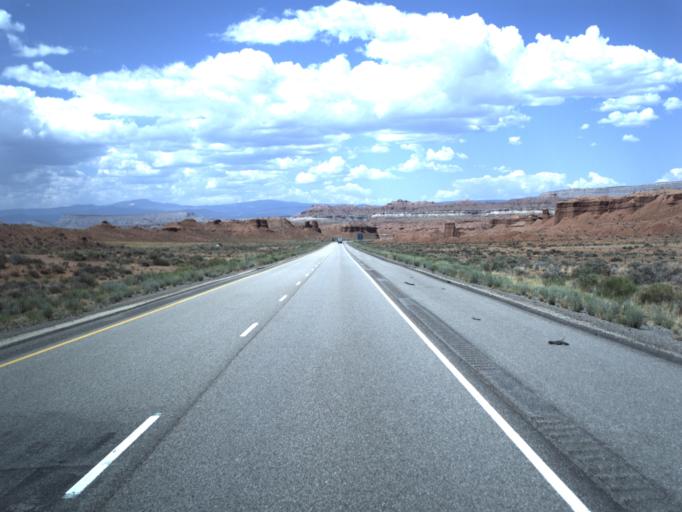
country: US
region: Utah
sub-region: Emery County
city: Ferron
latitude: 38.8472
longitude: -111.0355
